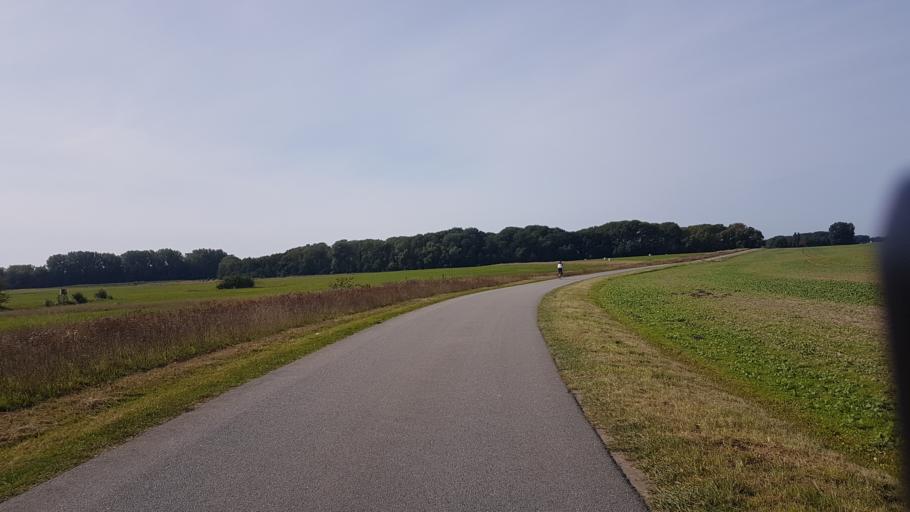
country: DE
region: Mecklenburg-Vorpommern
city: Gingst
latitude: 54.4197
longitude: 13.2395
